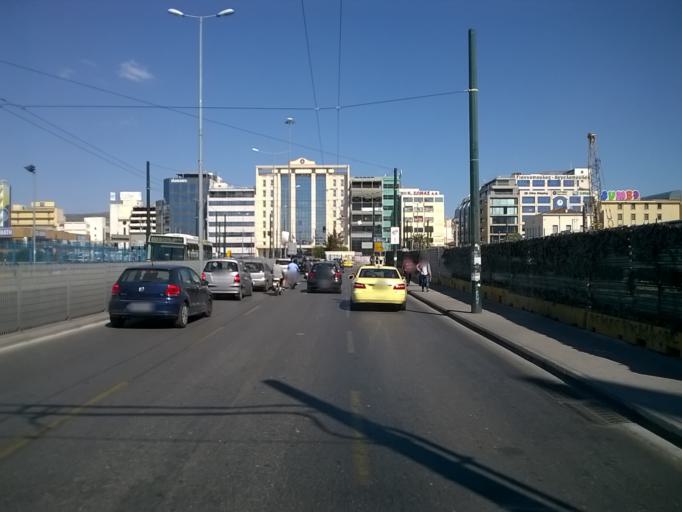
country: GR
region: Attica
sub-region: Nomos Attikis
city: Piraeus
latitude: 37.9479
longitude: 23.6420
